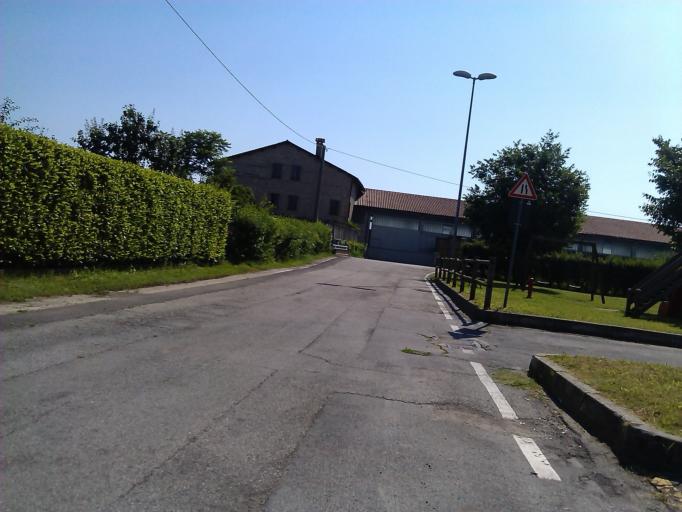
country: IT
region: Veneto
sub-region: Provincia di Vicenza
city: Casoni
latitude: 45.7440
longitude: 11.8133
